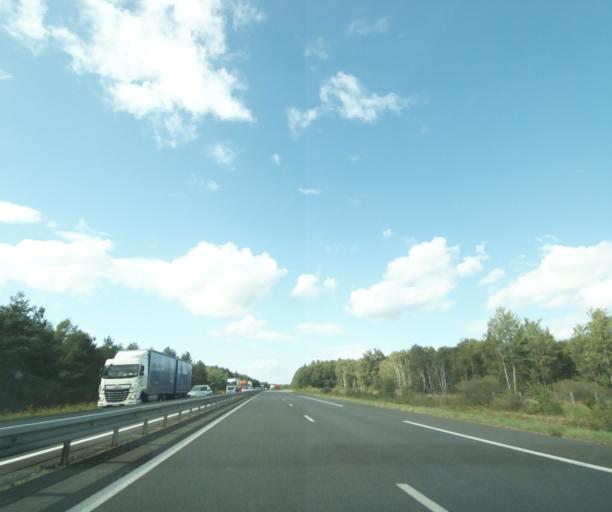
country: FR
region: Centre
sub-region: Departement du Loiret
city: Jouy-le-Potier
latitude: 47.7492
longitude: 1.8610
